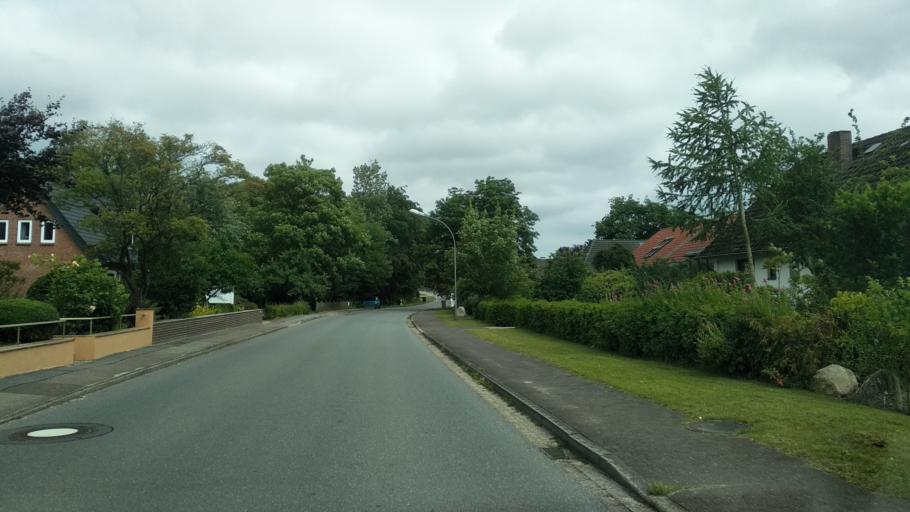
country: DE
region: Schleswig-Holstein
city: Neuberend
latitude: 54.5480
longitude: 9.5295
